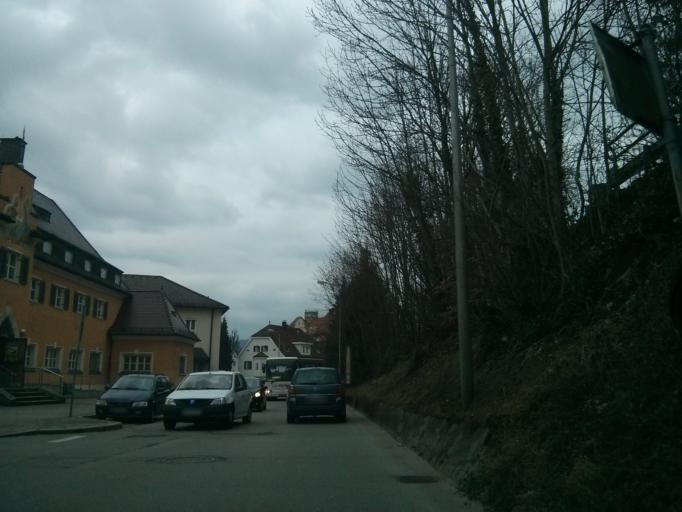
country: DE
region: Bavaria
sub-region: Lower Bavaria
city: Deggendorf
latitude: 48.8389
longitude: 12.9627
